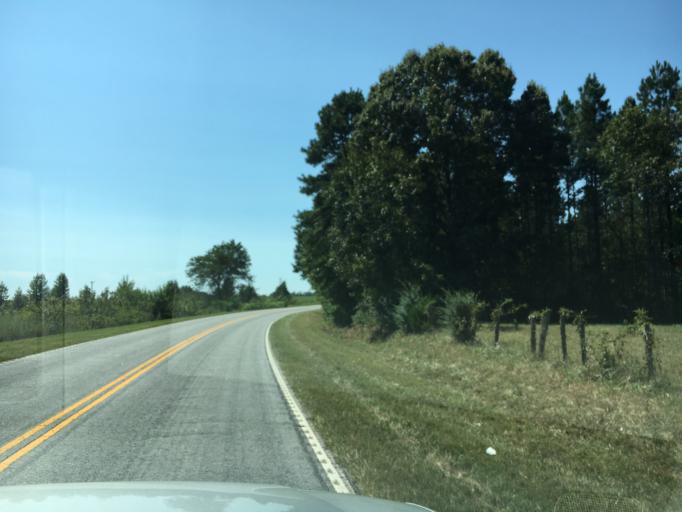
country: US
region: South Carolina
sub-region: Laurens County
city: Joanna
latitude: 34.3969
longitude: -81.8517
